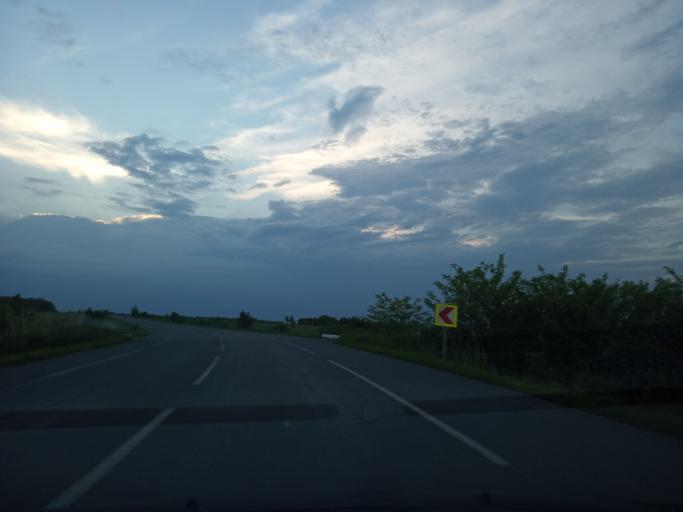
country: RO
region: Timis
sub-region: Oras Deta
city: Deta
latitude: 45.4056
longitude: 21.2371
